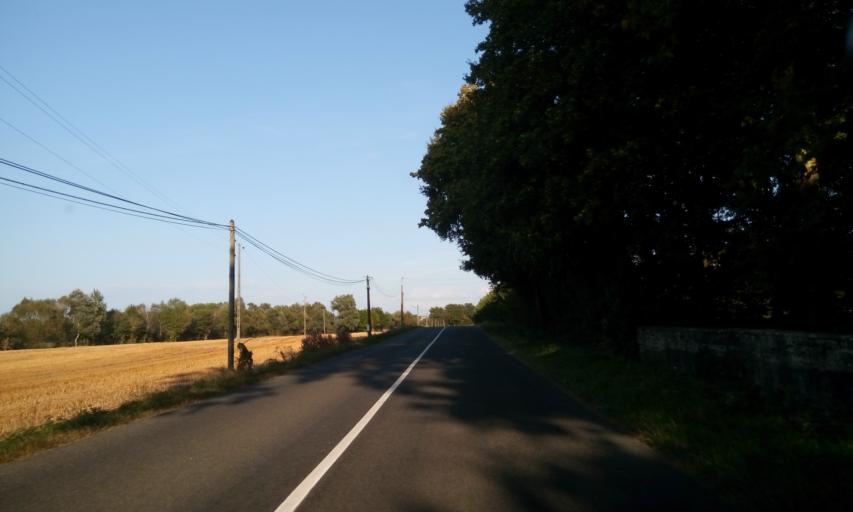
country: FR
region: Rhone-Alpes
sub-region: Departement de l'Ain
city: Chalamont
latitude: 45.9976
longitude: 5.1452
